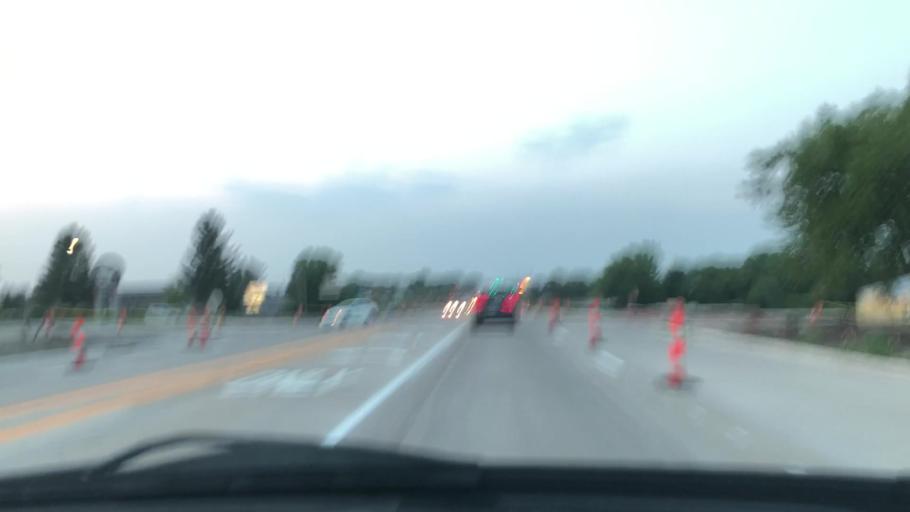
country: US
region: Iowa
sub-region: Johnson County
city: North Liberty
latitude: 41.7460
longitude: -91.6076
